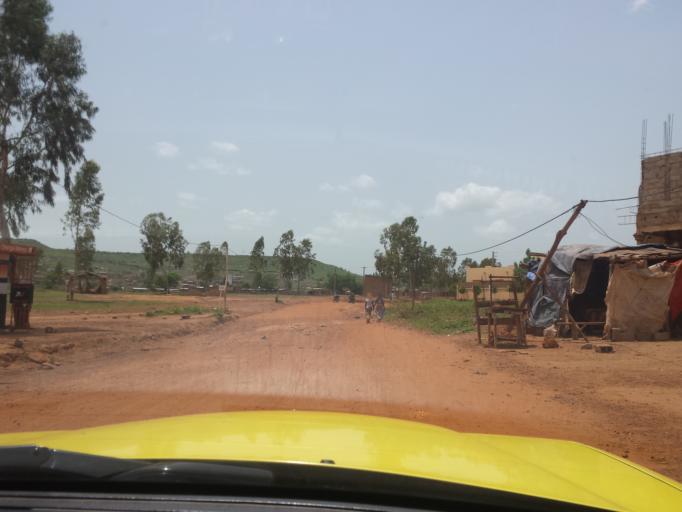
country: ML
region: Bamako
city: Bamako
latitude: 12.6128
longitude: -7.8856
